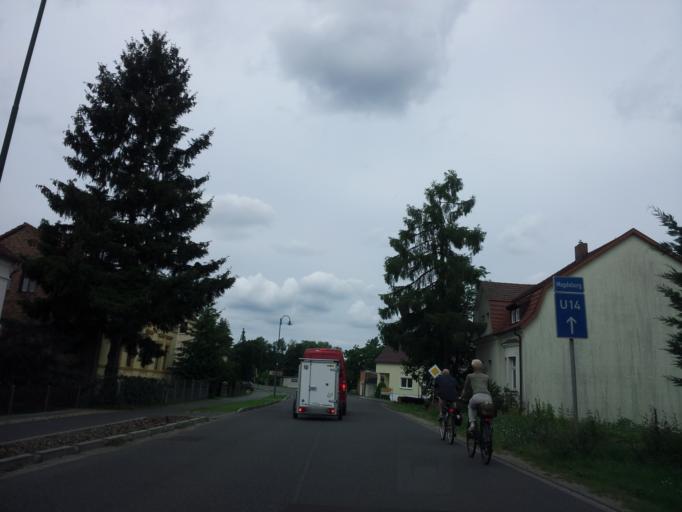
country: DE
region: Brandenburg
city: Trebbin
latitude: 52.2208
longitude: 13.1999
